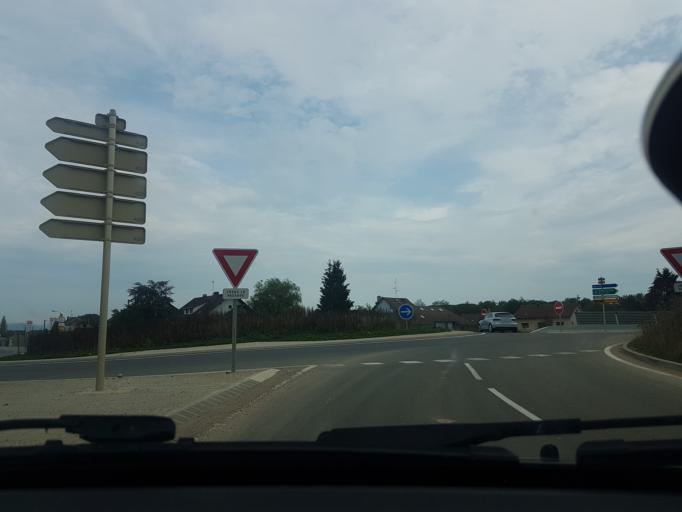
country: FR
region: Franche-Comte
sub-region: Territoire de Belfort
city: Andelnans
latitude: 47.5861
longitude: 6.8589
